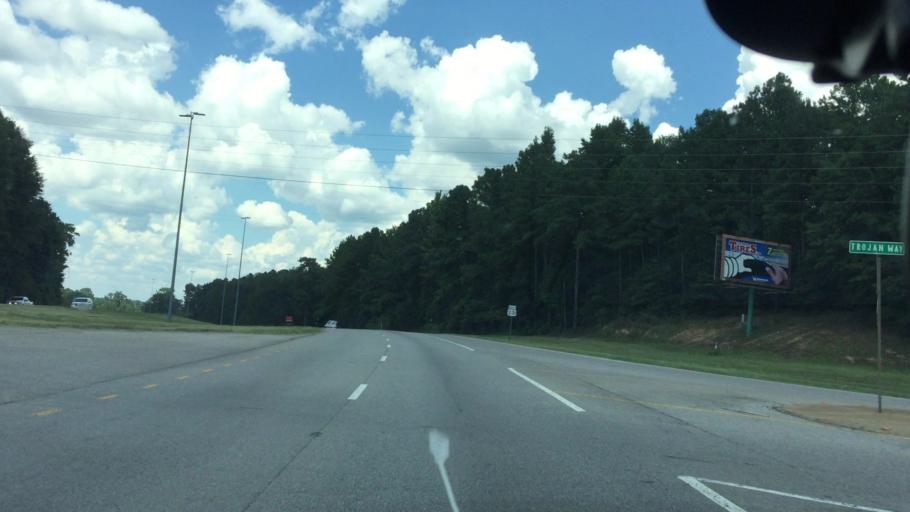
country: US
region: Alabama
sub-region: Pike County
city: Troy
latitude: 31.8325
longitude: -85.9908
